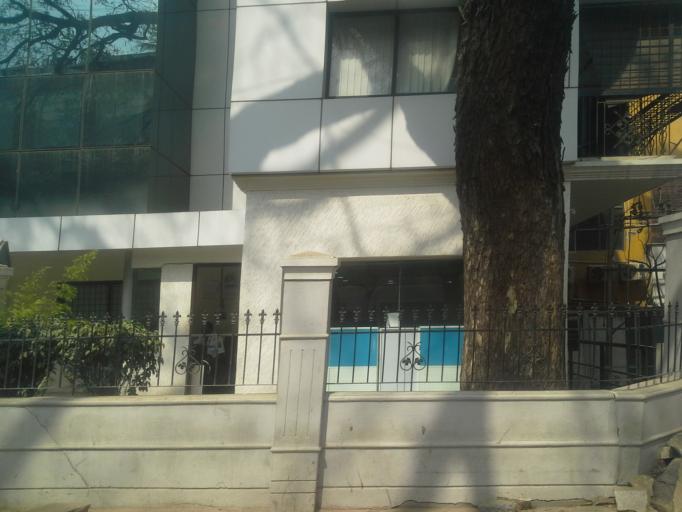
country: IN
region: Karnataka
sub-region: Bangalore Urban
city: Bangalore
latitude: 12.9748
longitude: 77.6198
